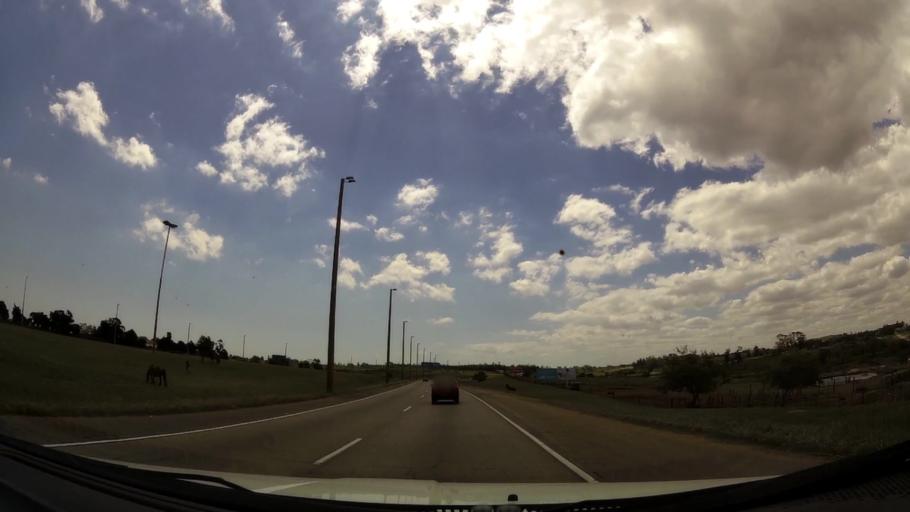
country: UY
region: Canelones
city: La Paz
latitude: -34.8207
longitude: -56.2534
